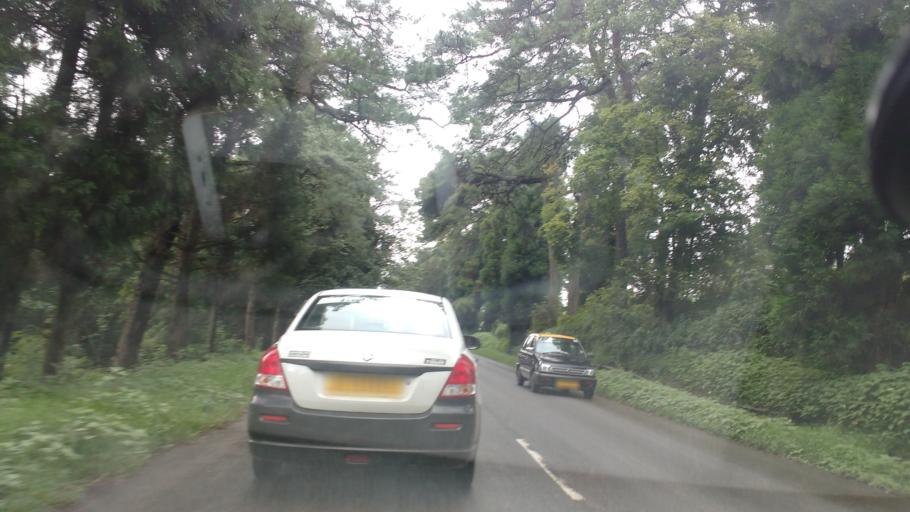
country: IN
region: Meghalaya
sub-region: East Khasi Hills
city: Shillong
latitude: 25.5534
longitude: 91.8450
